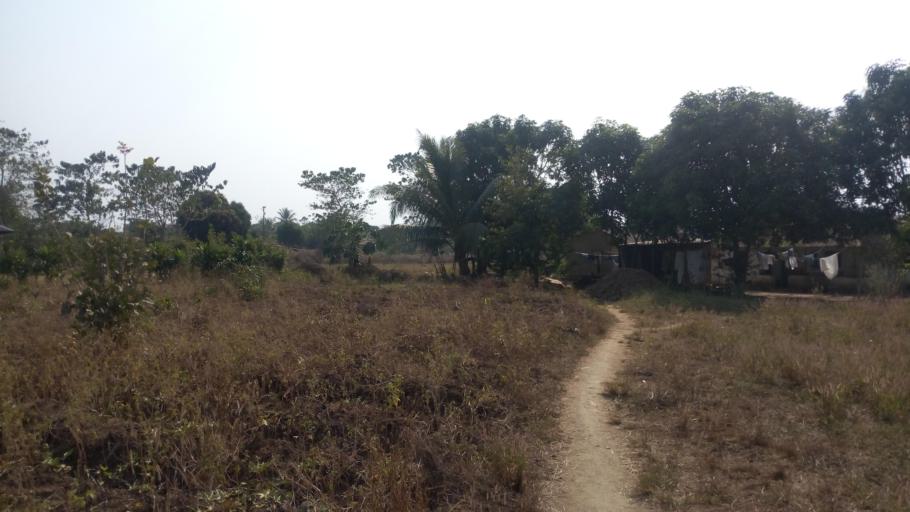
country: SL
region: Southern Province
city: Mogbwemo
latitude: 7.6170
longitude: -12.1787
